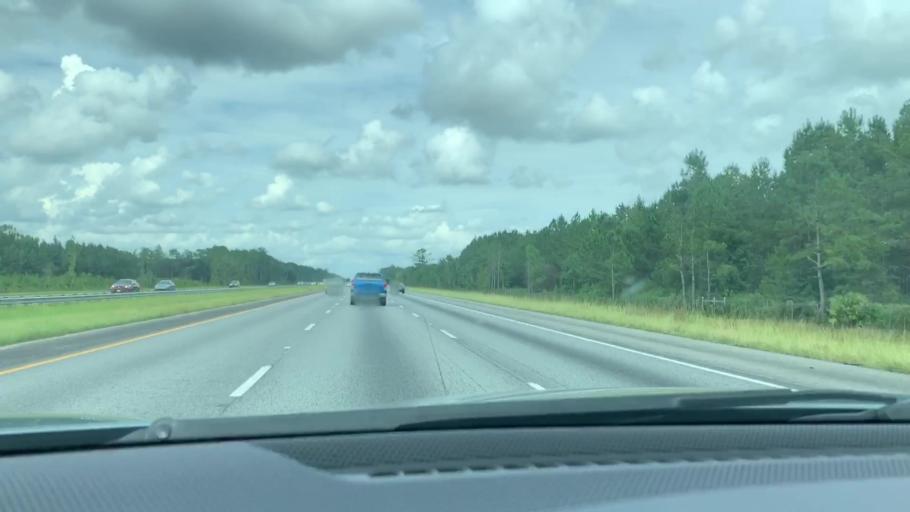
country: US
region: Georgia
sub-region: Liberty County
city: Midway
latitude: 31.6149
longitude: -81.4143
